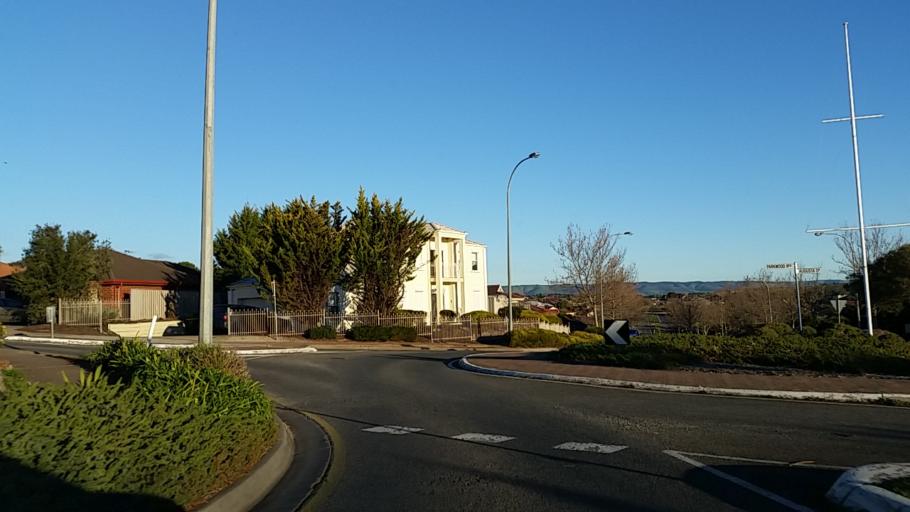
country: AU
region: South Australia
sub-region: Onkaparinga
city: Moana
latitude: -35.2038
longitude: 138.4878
